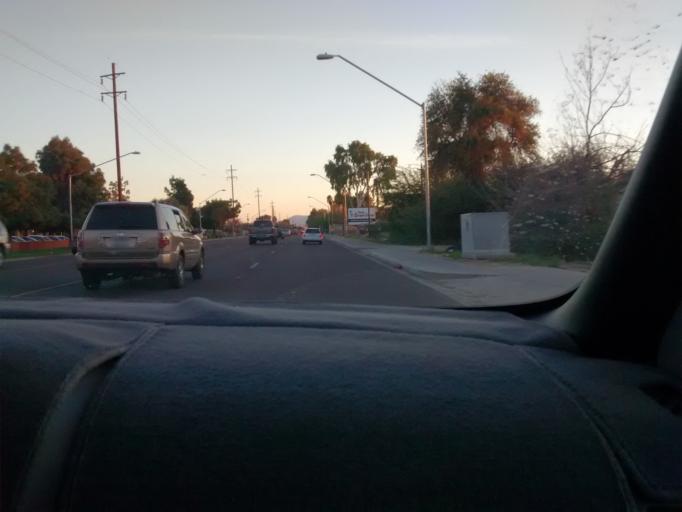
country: US
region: Arizona
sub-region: Maricopa County
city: Glendale
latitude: 33.5289
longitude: -112.2032
